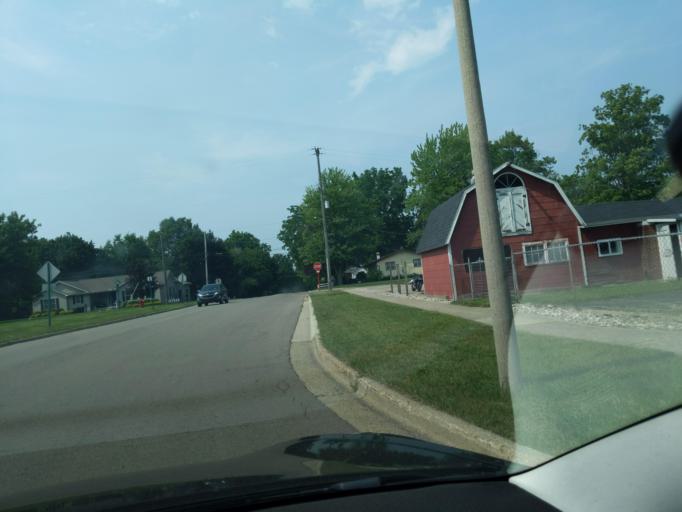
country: US
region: Michigan
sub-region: Clinton County
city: Saint Johns
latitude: 42.9966
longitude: -84.5665
